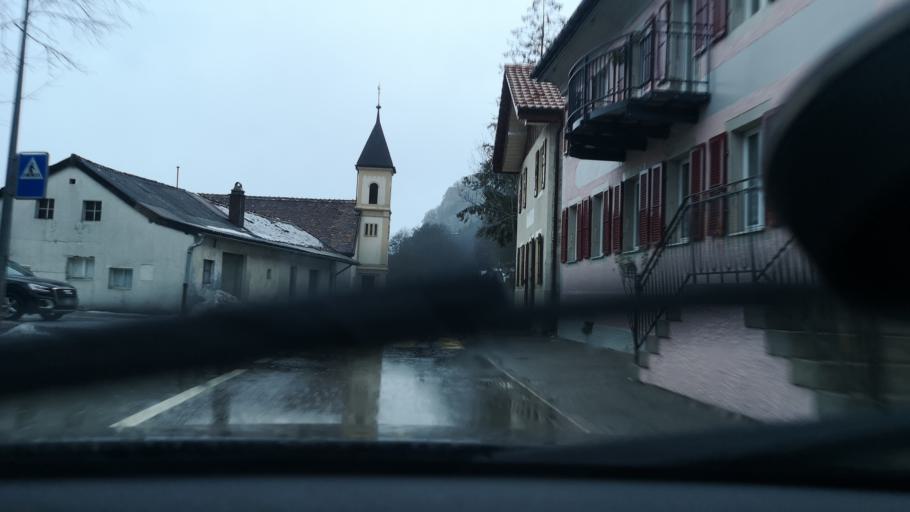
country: CH
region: Neuchatel
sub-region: Le Locle District
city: Les Ponts-de-Martel
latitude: 46.9559
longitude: 6.7479
